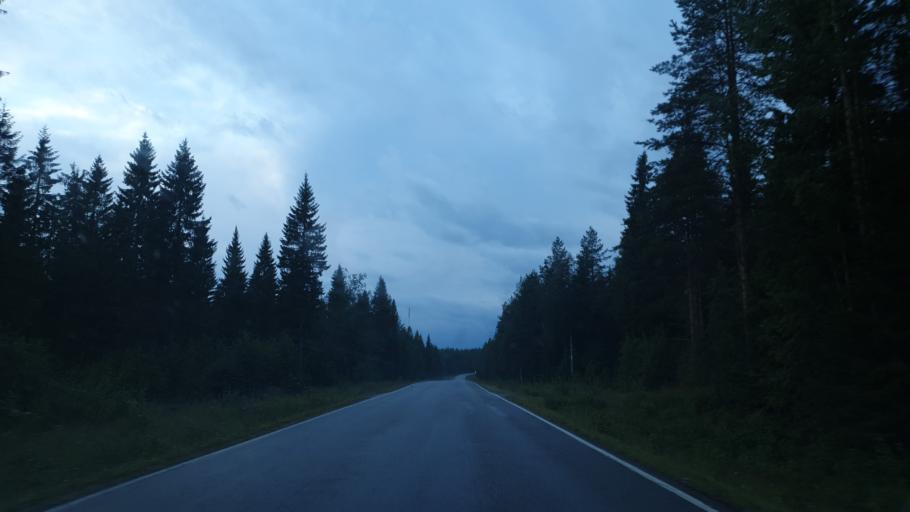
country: FI
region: Kainuu
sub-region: Kehys-Kainuu
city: Kuhmo
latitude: 63.9566
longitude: 29.7098
